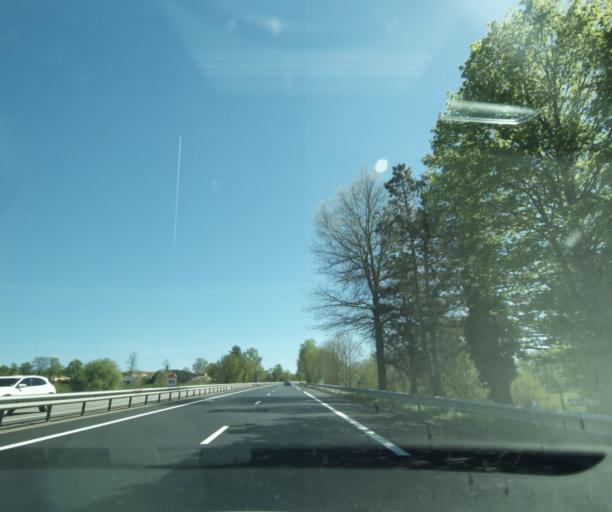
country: FR
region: Limousin
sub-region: Departement de la Haute-Vienne
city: Boisseuil
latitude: 45.7667
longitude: 1.3239
